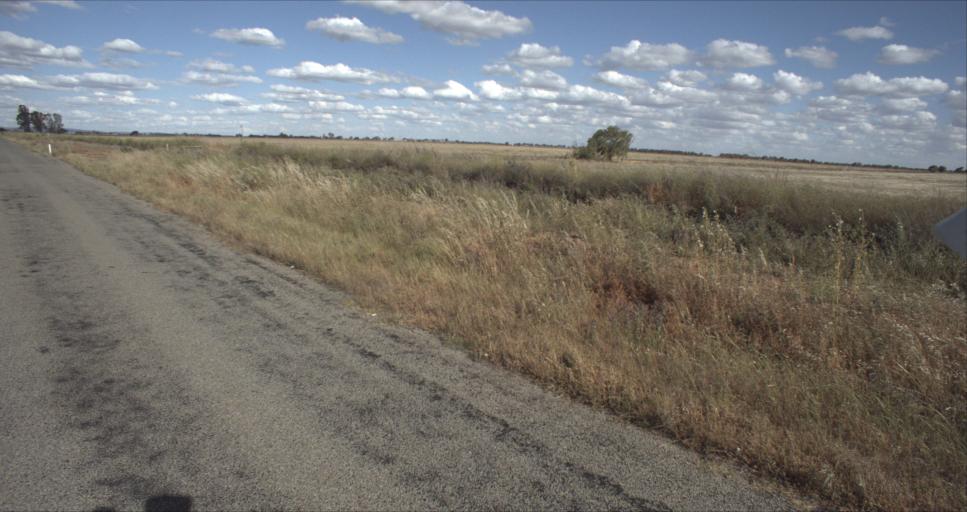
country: AU
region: New South Wales
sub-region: Leeton
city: Leeton
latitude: -34.4412
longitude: 146.2316
